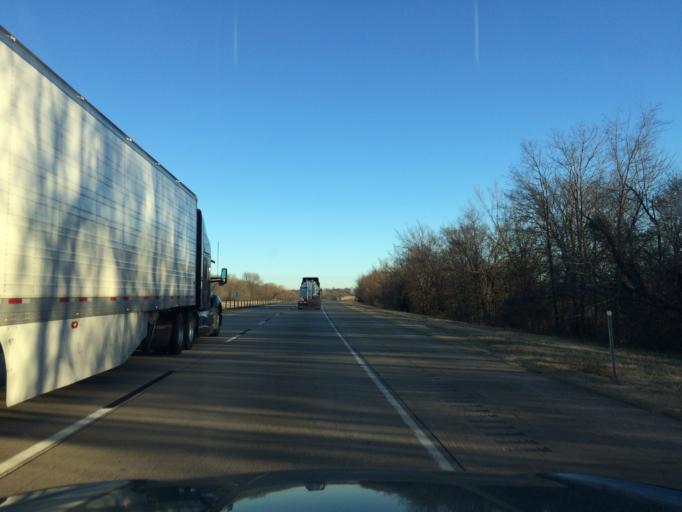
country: US
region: Oklahoma
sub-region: Sequoyah County
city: Vian
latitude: 35.4852
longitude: -94.9625
